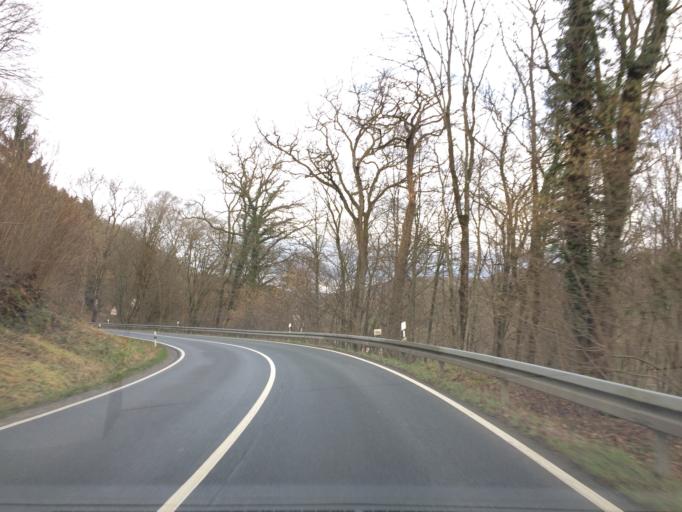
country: DE
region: Hesse
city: Weilmunster
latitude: 50.3730
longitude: 8.3961
